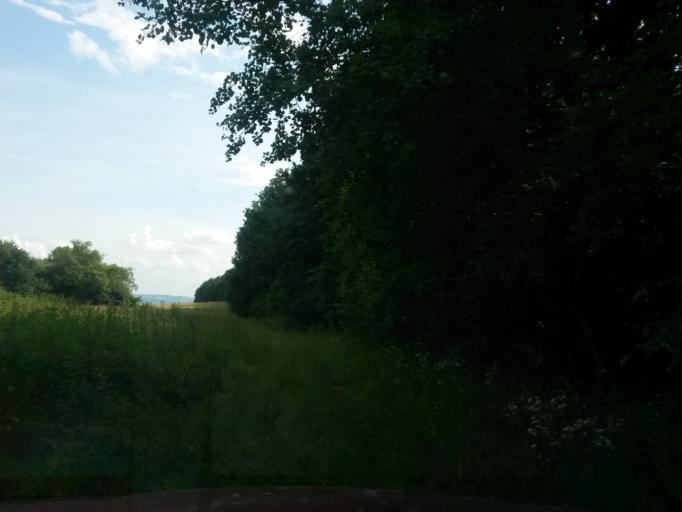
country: SK
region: Kosicky
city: Moldava nad Bodvou
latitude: 48.6221
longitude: 21.0991
